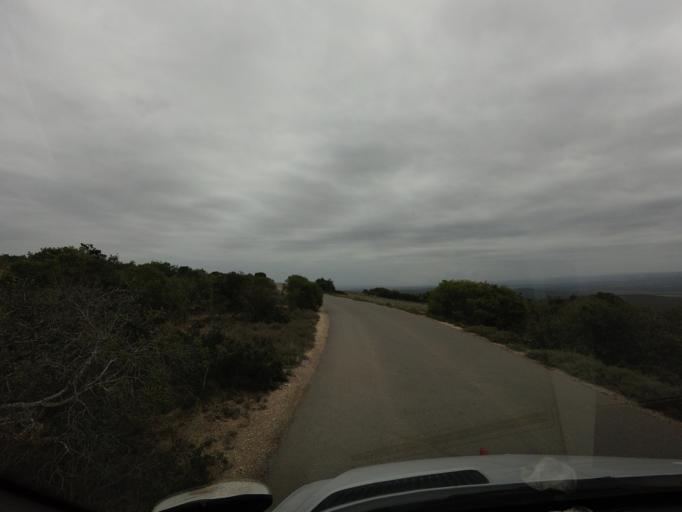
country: ZA
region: Eastern Cape
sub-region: Cacadu District Municipality
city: Kirkwood
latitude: -33.4632
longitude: 25.7833
